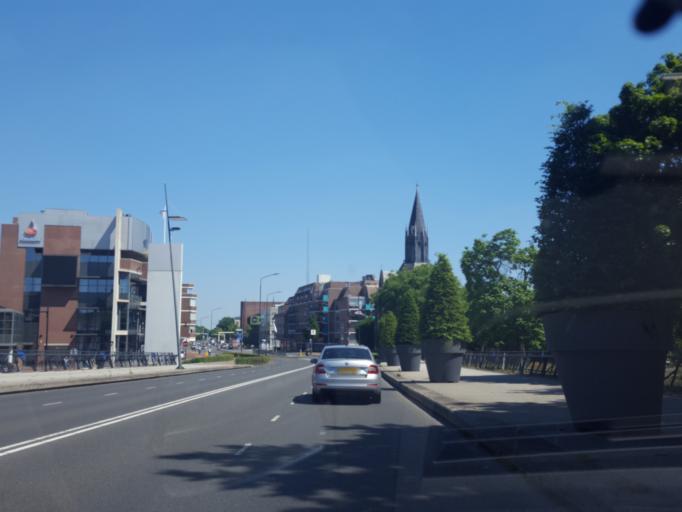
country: NL
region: North Brabant
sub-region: Gemeente Helmond
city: Helmond
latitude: 51.4781
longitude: 5.6538
